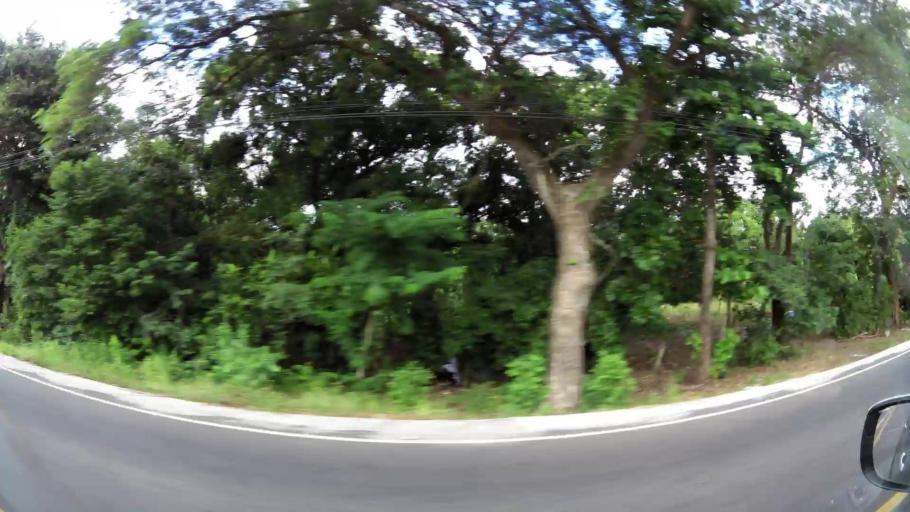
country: CR
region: Guanacaste
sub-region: Canton de Nicoya
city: Nicoya
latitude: 10.1440
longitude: -85.3250
